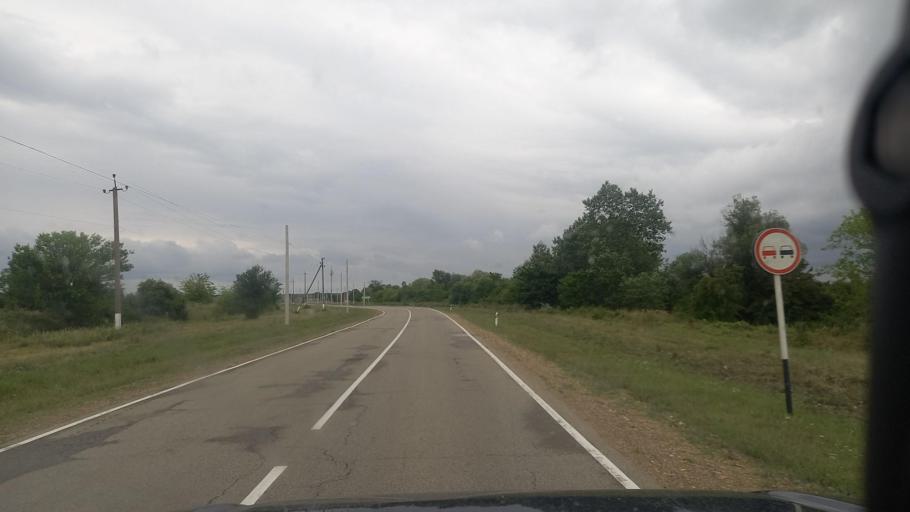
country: RU
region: Adygeya
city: Adygeysk
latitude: 44.8850
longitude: 39.2513
